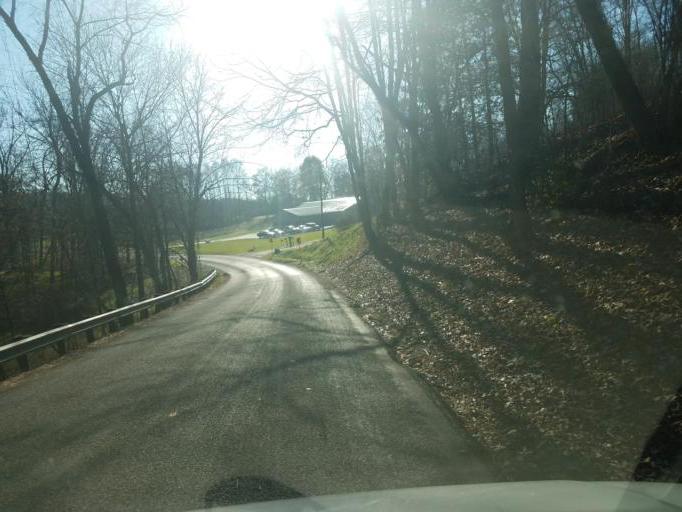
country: US
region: Ohio
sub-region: Sandusky County
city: Bellville
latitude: 40.6367
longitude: -82.5289
